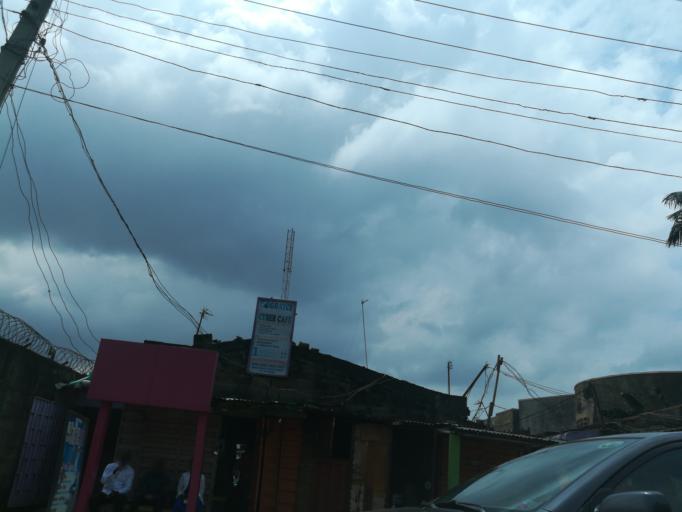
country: NG
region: Lagos
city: Oshodi
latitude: 6.5501
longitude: 3.3309
